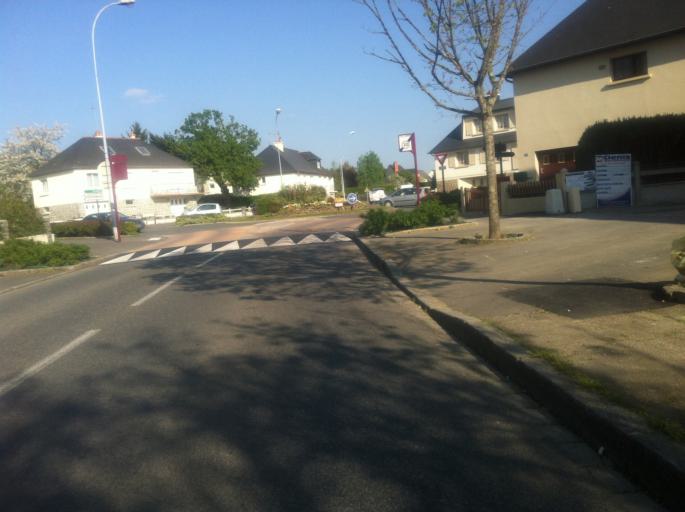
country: FR
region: Brittany
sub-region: Departement d'Ille-et-Vilaine
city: Bruz
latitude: 48.0232
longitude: -1.7369
